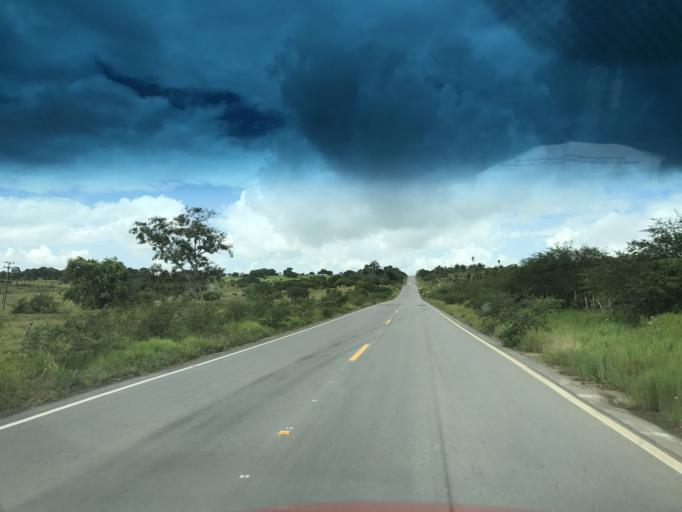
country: BR
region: Bahia
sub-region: Conceicao Do Almeida
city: Conceicao do Almeida
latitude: -12.6877
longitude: -39.2500
